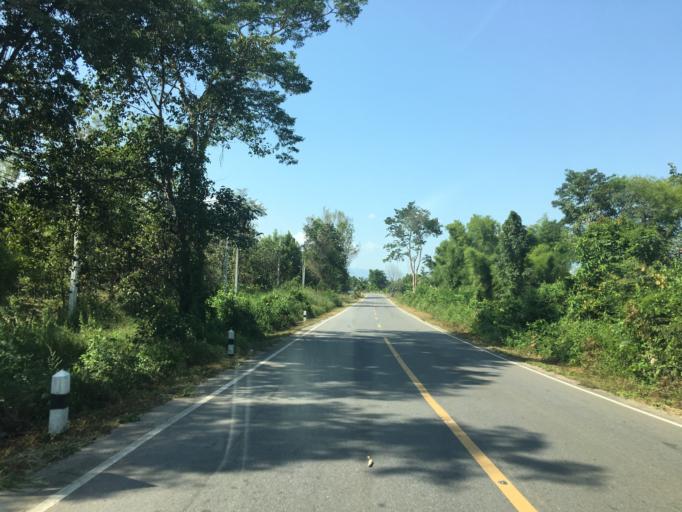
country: TH
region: Phayao
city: Chiang Muan
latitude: 18.8658
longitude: 100.3059
